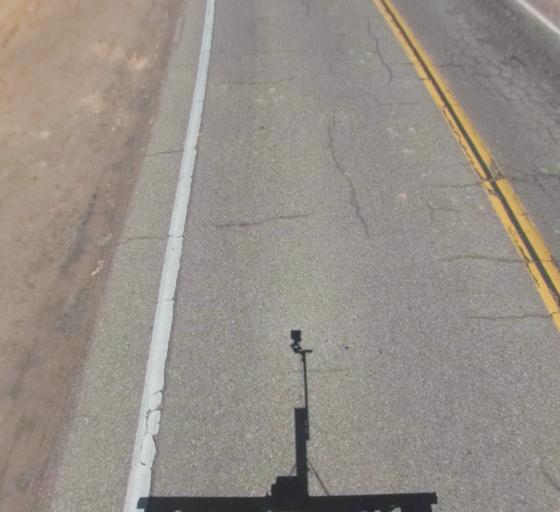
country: US
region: California
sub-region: Fresno County
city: Biola
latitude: 36.8545
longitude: -119.9094
